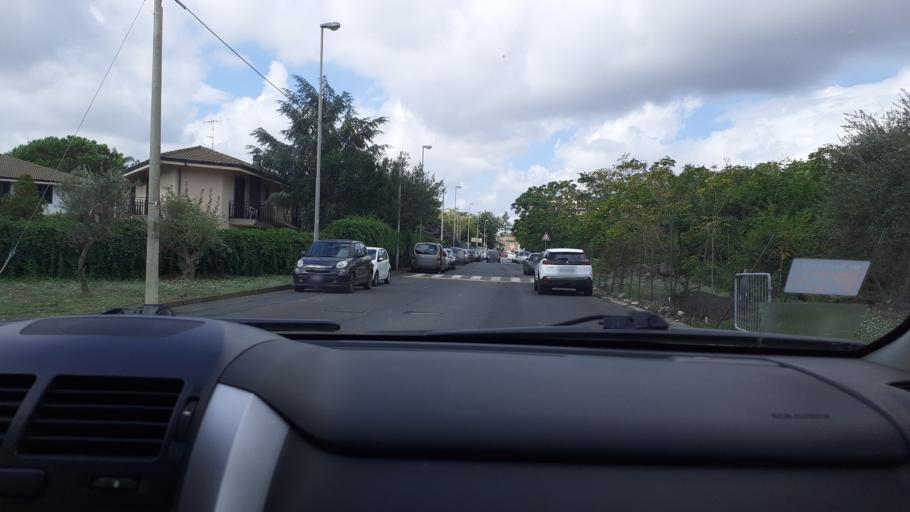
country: IT
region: Sicily
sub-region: Catania
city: San Giovanni la Punta
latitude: 37.5808
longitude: 15.0995
